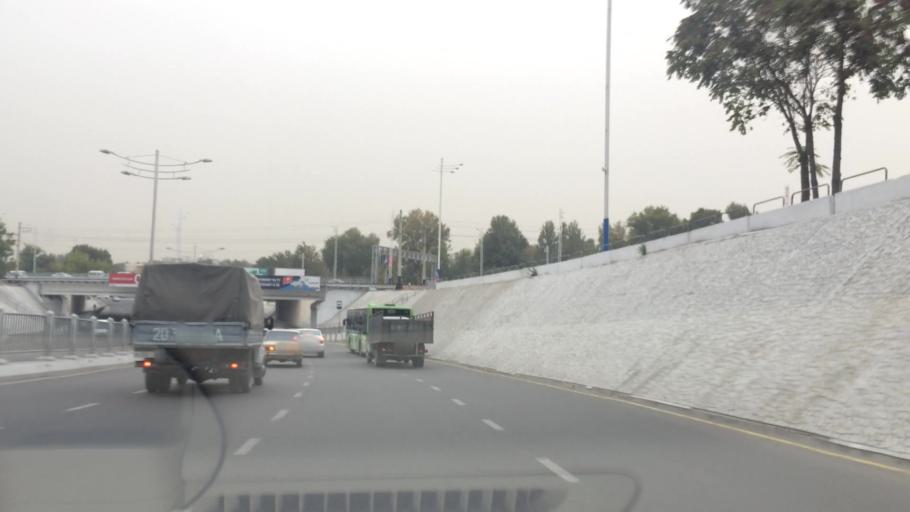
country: UZ
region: Toshkent Shahri
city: Tashkent
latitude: 41.3070
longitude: 69.3037
